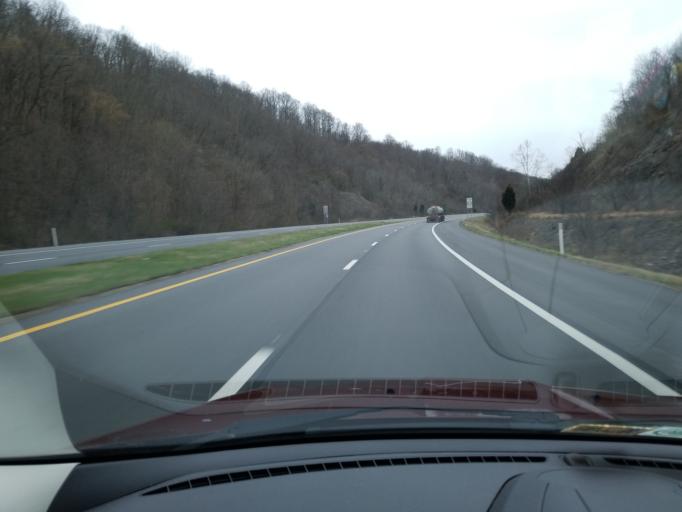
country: US
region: Virginia
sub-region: Giles County
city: Narrows
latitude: 37.3650
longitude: -80.8701
